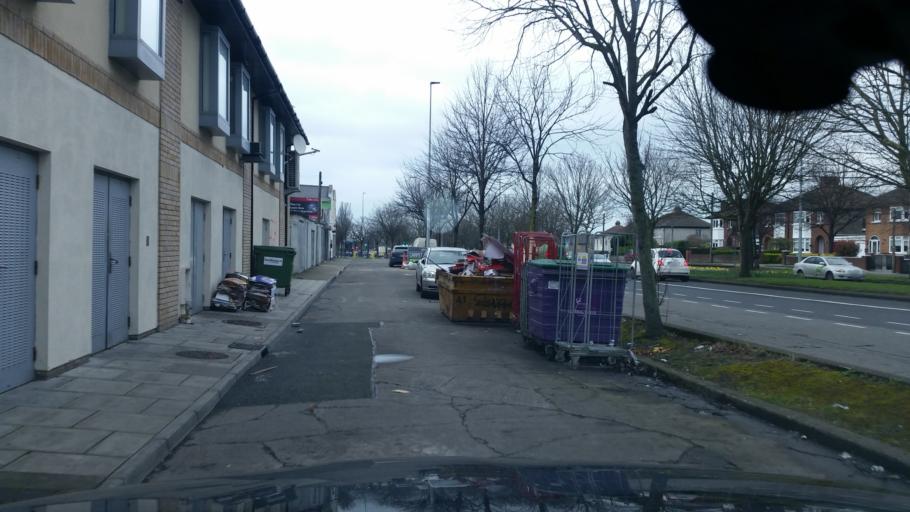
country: IE
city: Coolock
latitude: 53.3871
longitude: -6.2010
